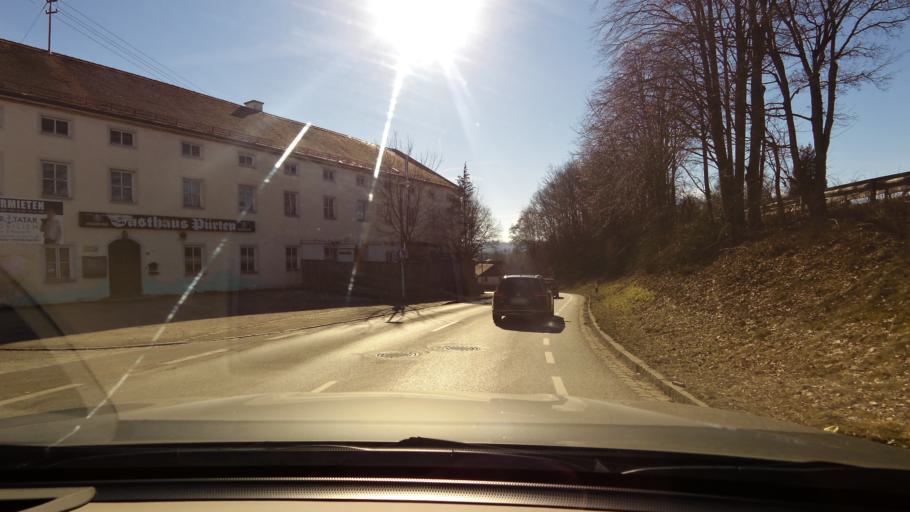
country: DE
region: Bavaria
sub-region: Upper Bavaria
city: Kraiburg am Inn
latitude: 48.2021
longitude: 12.4241
